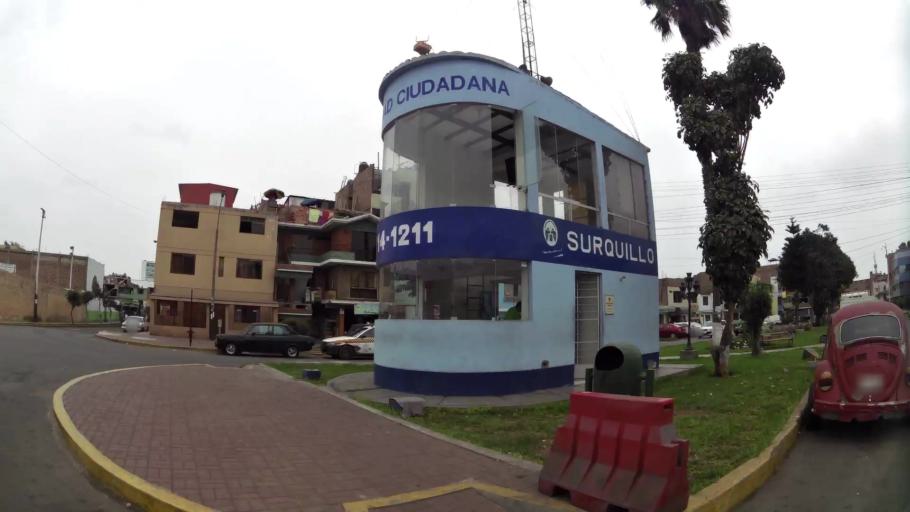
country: PE
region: Lima
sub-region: Lima
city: Surco
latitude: -12.1089
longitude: -77.0116
